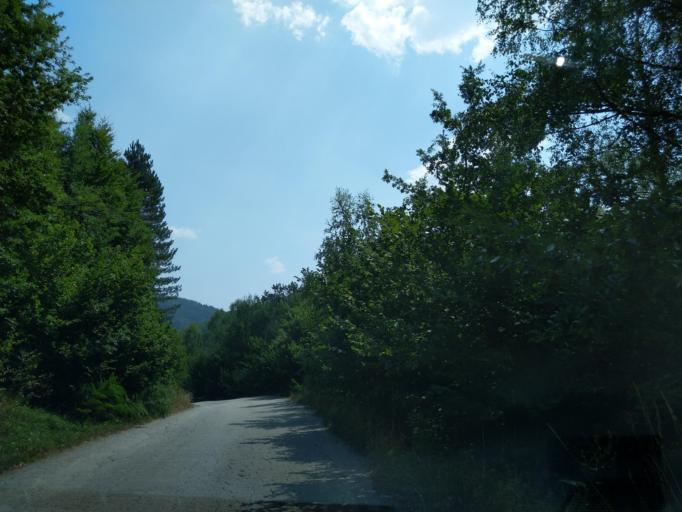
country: RS
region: Central Serbia
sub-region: Zlatiborski Okrug
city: Prijepolje
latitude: 43.3313
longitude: 19.5700
